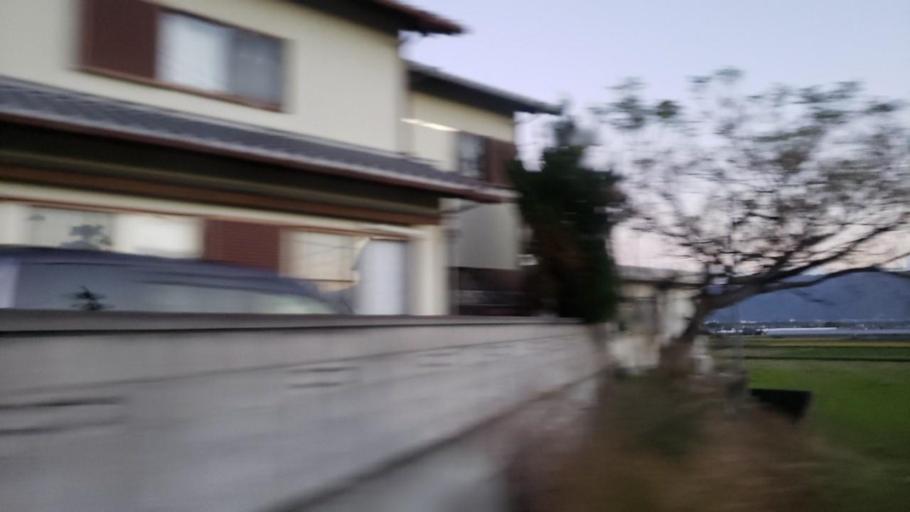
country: JP
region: Tokushima
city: Kamojimacho-jogejima
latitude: 34.1090
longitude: 134.3283
